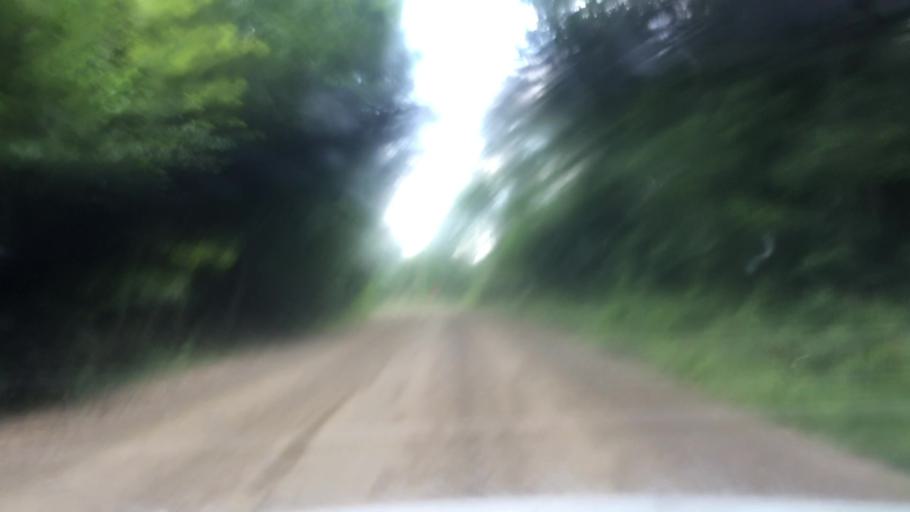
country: US
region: Maine
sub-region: Waldo County
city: Searsmont
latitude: 44.4034
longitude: -69.2757
